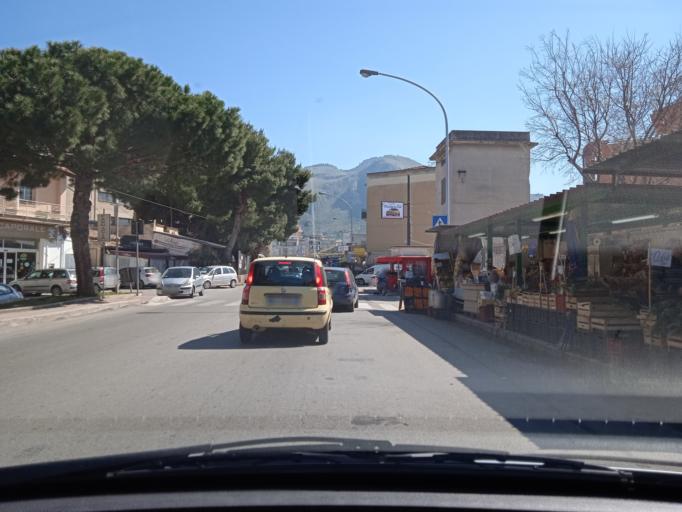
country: IT
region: Sicily
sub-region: Palermo
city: Villabate
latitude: 38.0831
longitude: 13.4340
